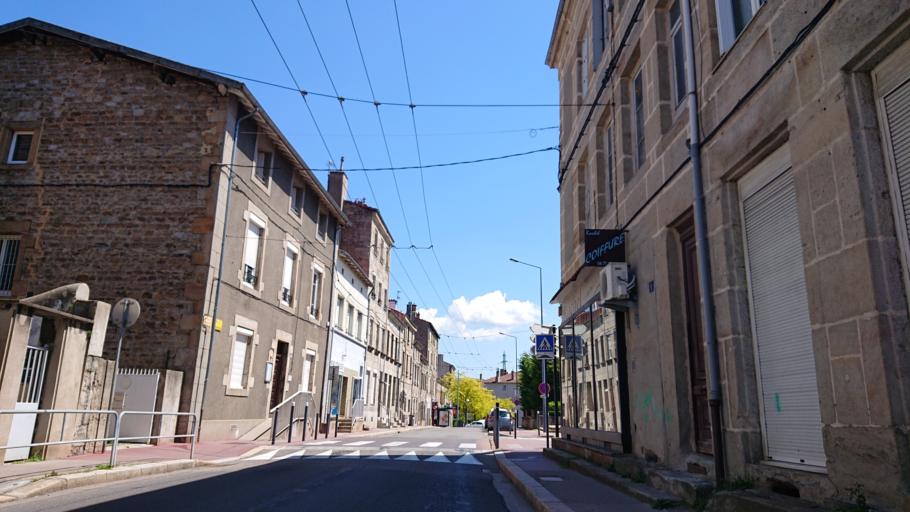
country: FR
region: Rhone-Alpes
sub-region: Departement de la Loire
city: Saint-Genest-Lerpt
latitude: 45.4455
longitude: 4.3630
